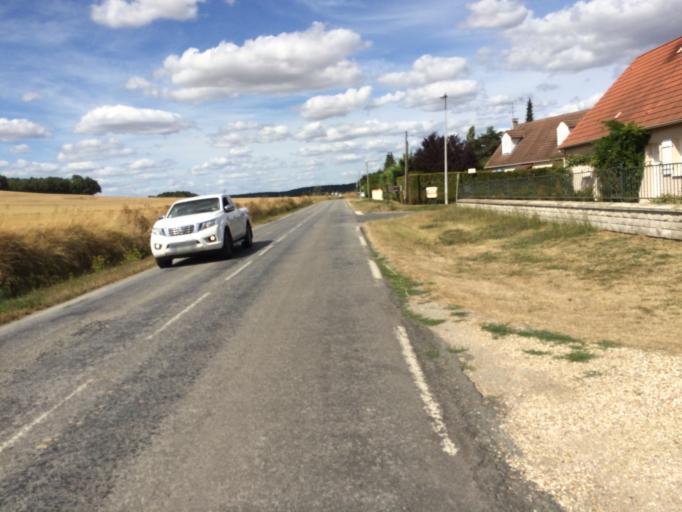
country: FR
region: Ile-de-France
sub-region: Departement de l'Essonne
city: Maisse
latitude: 48.4059
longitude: 2.3792
